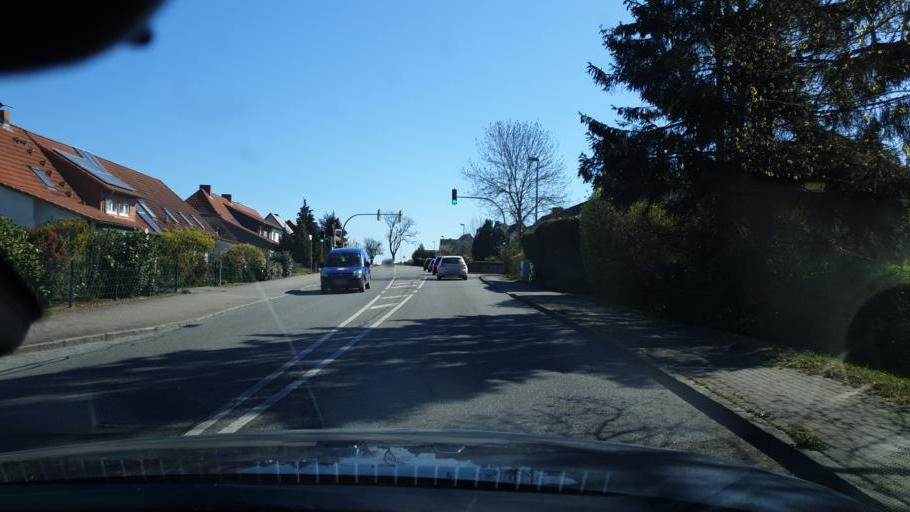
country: DE
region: Mecklenburg-Vorpommern
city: Leezen
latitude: 53.6865
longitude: 11.4847
